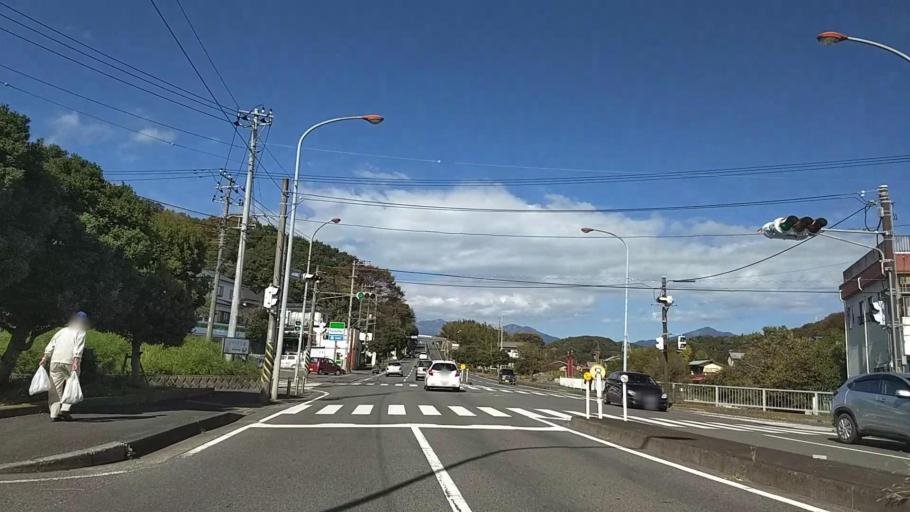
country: JP
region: Kanagawa
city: Ninomiya
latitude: 35.3161
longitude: 139.2422
